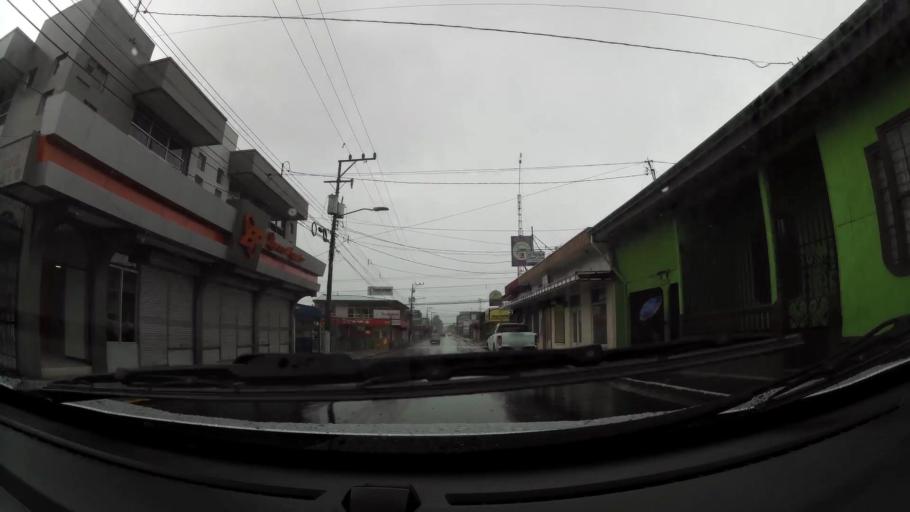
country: CR
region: Cartago
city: Cartago
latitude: 9.8661
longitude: -83.9250
